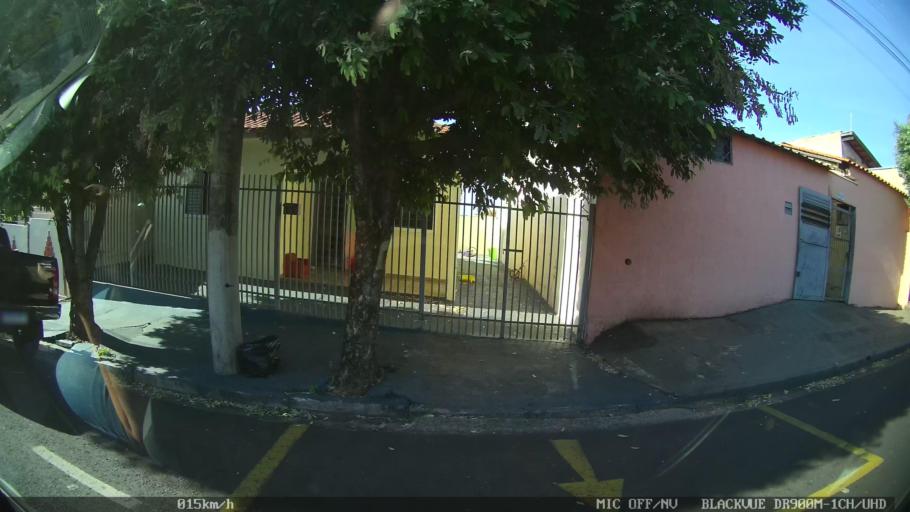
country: BR
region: Sao Paulo
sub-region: Sao Jose Do Rio Preto
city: Sao Jose do Rio Preto
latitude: -20.7810
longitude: -49.3612
